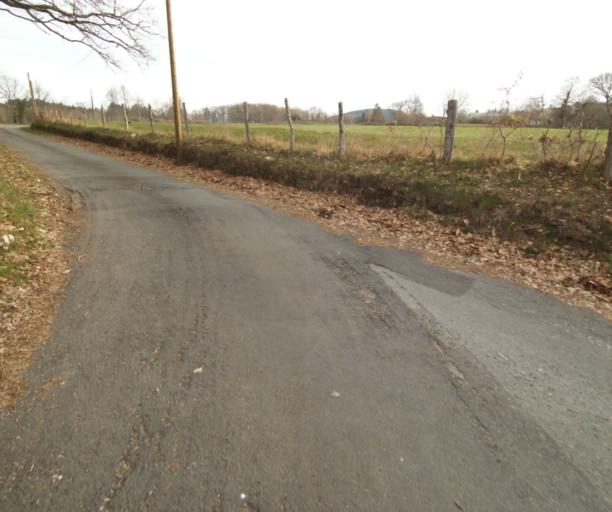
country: FR
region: Limousin
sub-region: Departement de la Correze
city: Treignac
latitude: 45.4437
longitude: 1.8091
